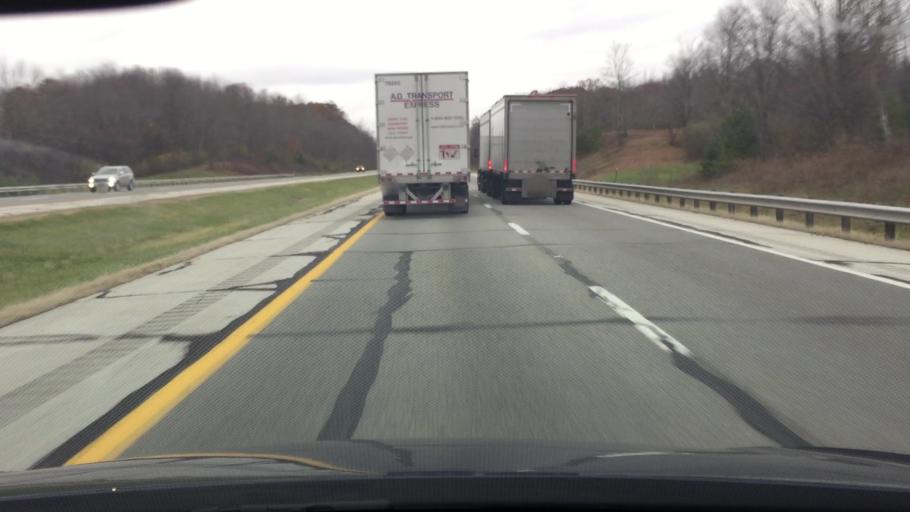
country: US
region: Ohio
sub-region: Mahoning County
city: Canfield
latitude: 41.0590
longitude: -80.7793
